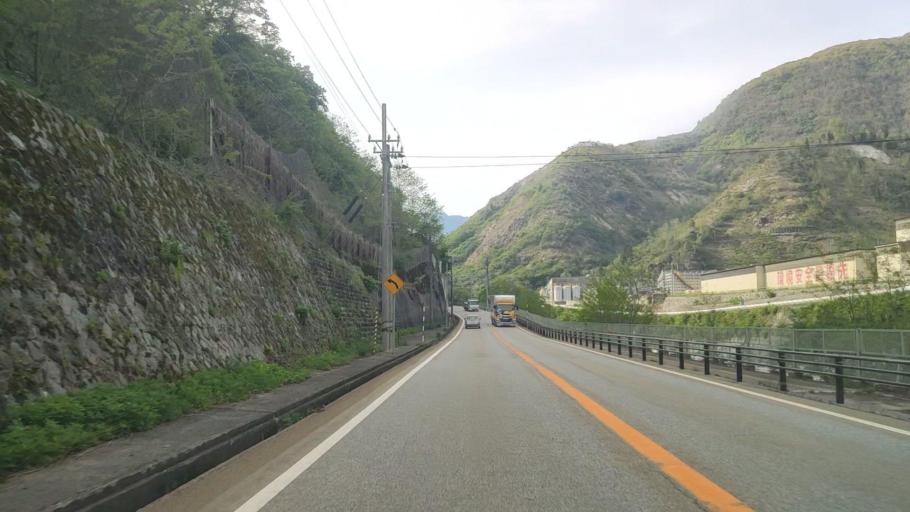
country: JP
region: Gifu
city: Takayama
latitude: 36.3461
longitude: 137.2943
